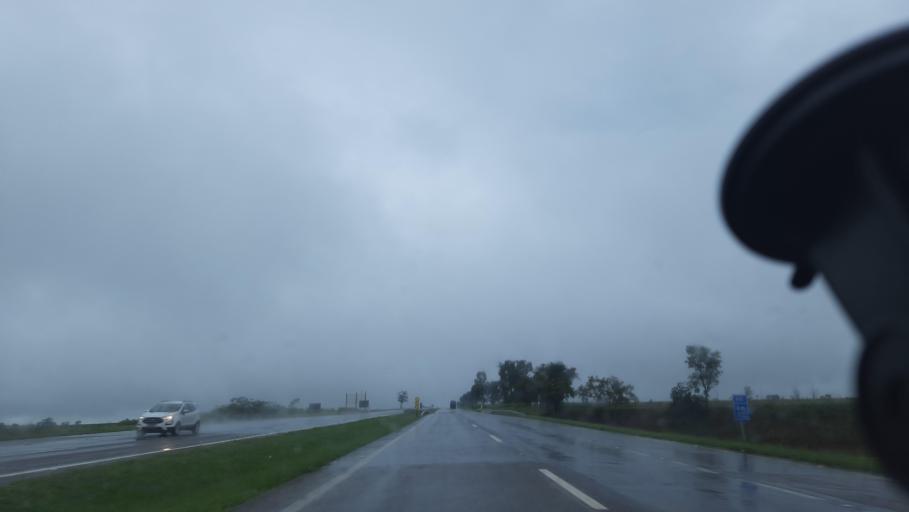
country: BR
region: Sao Paulo
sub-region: Aguai
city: Aguai
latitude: -22.0151
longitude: -47.0355
